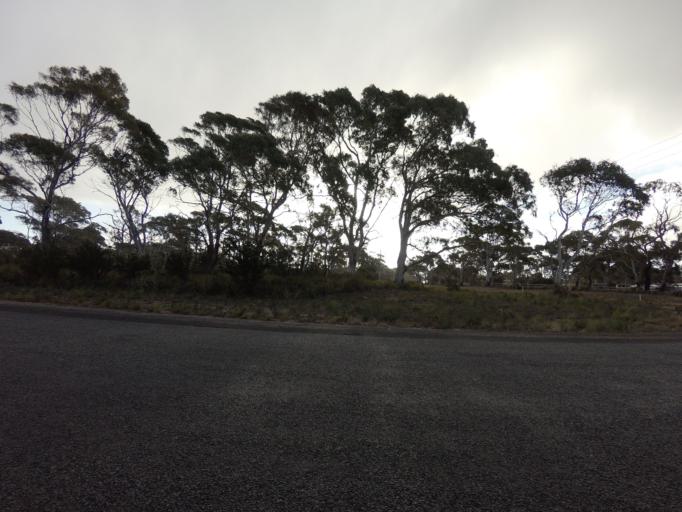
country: AU
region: Tasmania
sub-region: Break O'Day
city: St Helens
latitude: -42.0986
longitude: 148.0882
